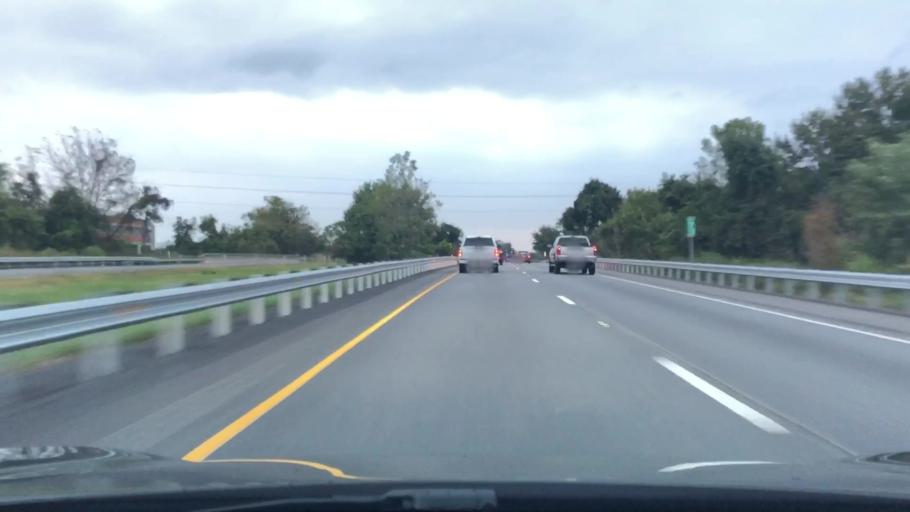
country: US
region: Pennsylvania
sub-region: Bucks County
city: Woodside
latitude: 40.2189
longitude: -74.8794
